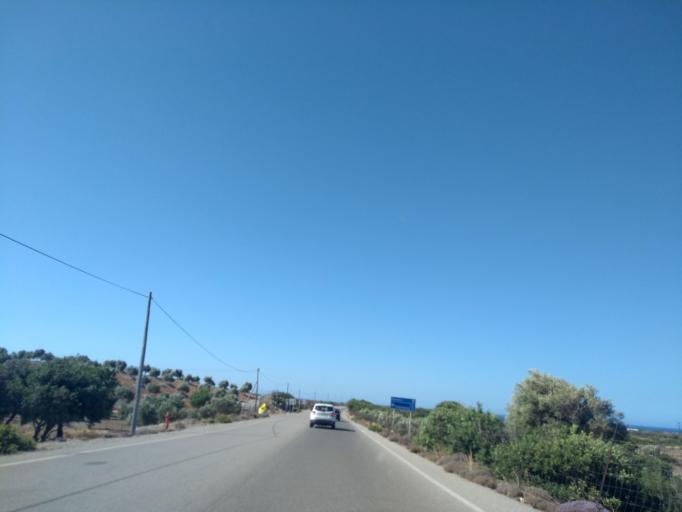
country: GR
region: Crete
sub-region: Nomos Chanias
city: Palaiochora
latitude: 35.2847
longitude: 23.5482
